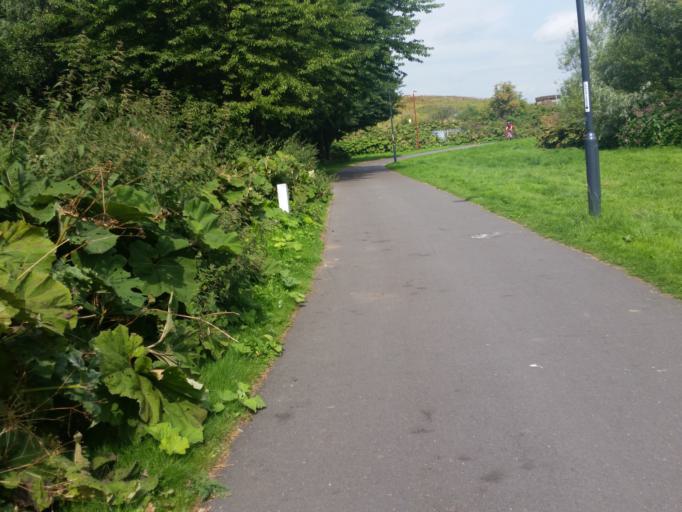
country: GB
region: England
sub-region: Derby
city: Derby
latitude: 52.9102
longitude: -1.4405
